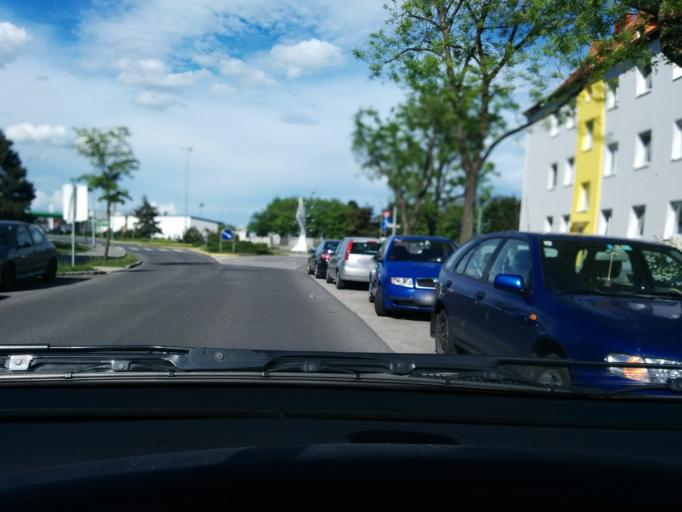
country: AT
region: Lower Austria
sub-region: Politischer Bezirk Wiener Neustadt
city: Theresienfeld
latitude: 47.8275
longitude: 16.2430
